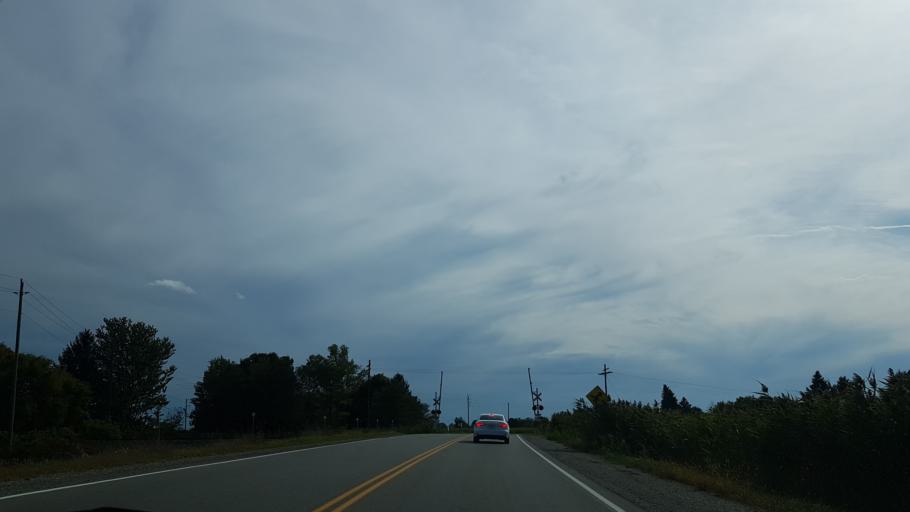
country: CA
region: Ontario
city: Delaware
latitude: 42.9804
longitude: -81.3861
